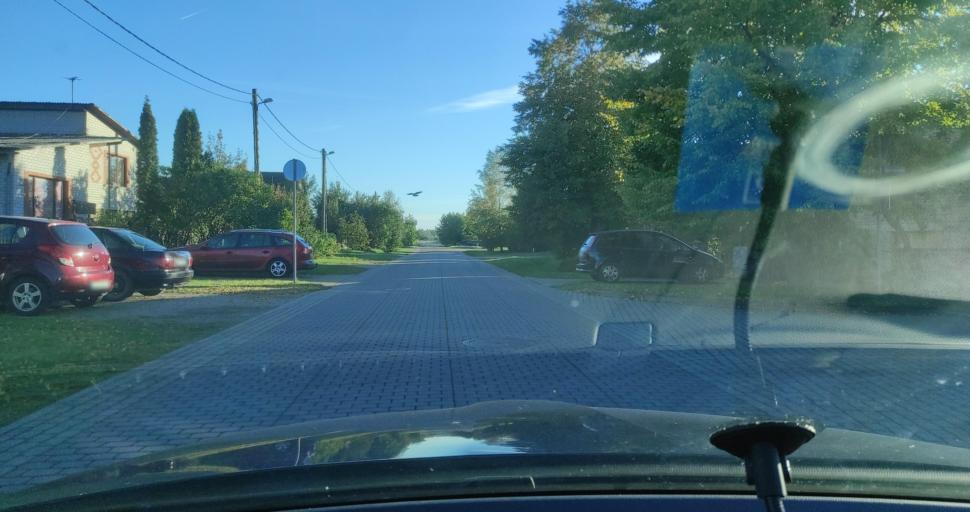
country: LV
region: Ventspils
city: Ventspils
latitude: 57.3712
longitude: 21.5760
